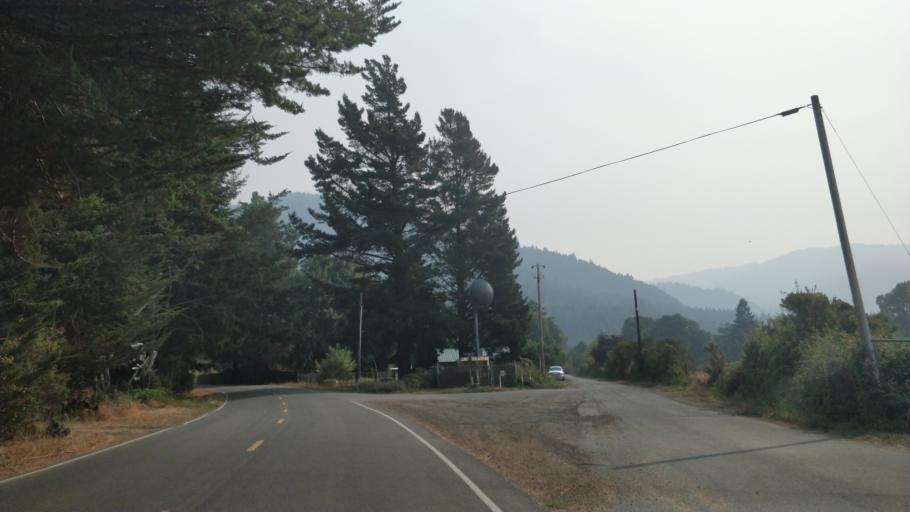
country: US
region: California
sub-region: Humboldt County
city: Rio Dell
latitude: 40.3195
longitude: -124.2858
